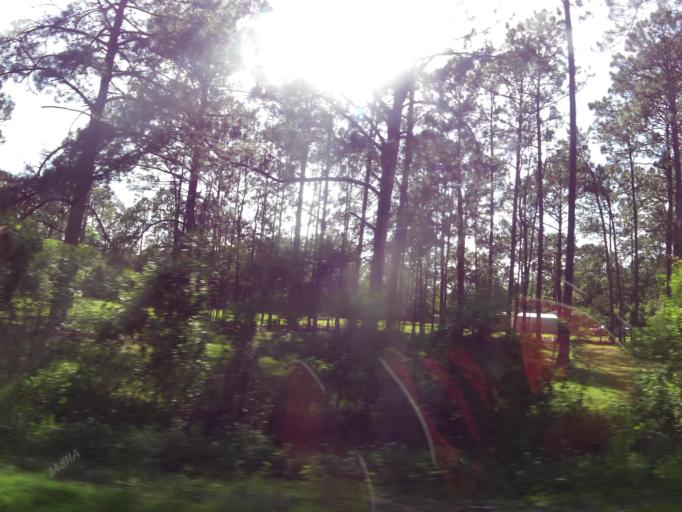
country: US
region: Florida
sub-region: Nassau County
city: Hilliard
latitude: 30.6468
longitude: -81.9031
